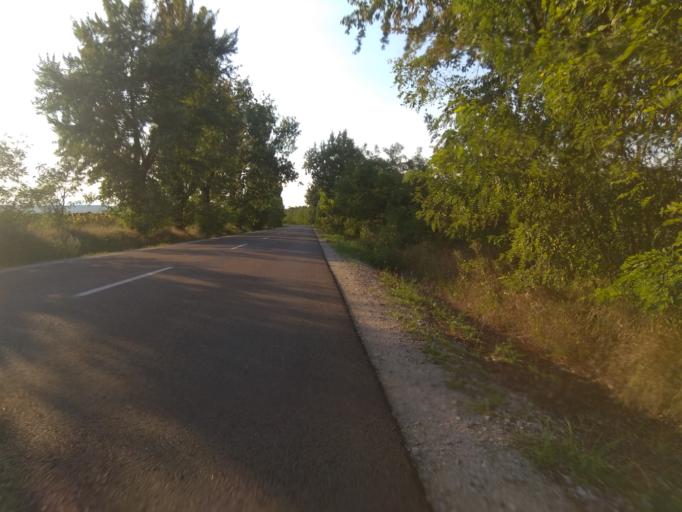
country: HU
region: Borsod-Abauj-Zemplen
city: Nyekladhaza
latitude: 47.9619
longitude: 20.8630
